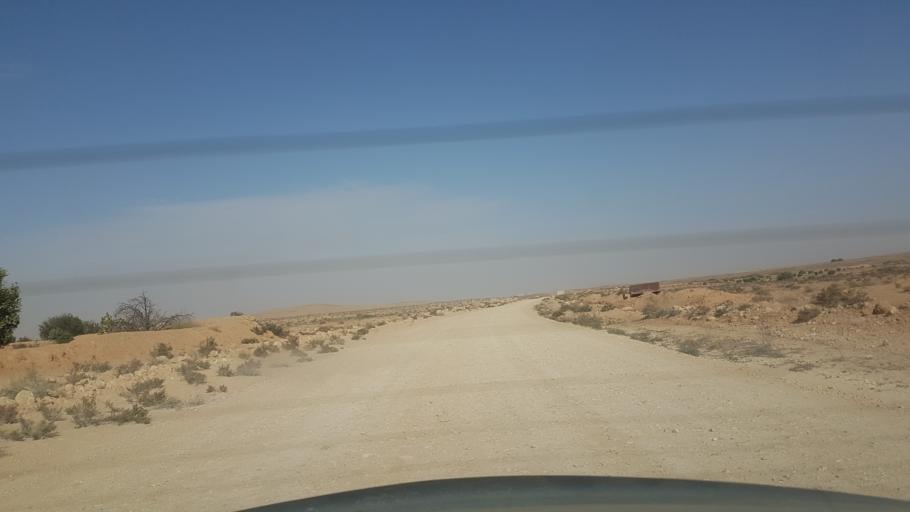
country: TN
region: Qabis
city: El Hamma
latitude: 33.6638
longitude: 9.7353
